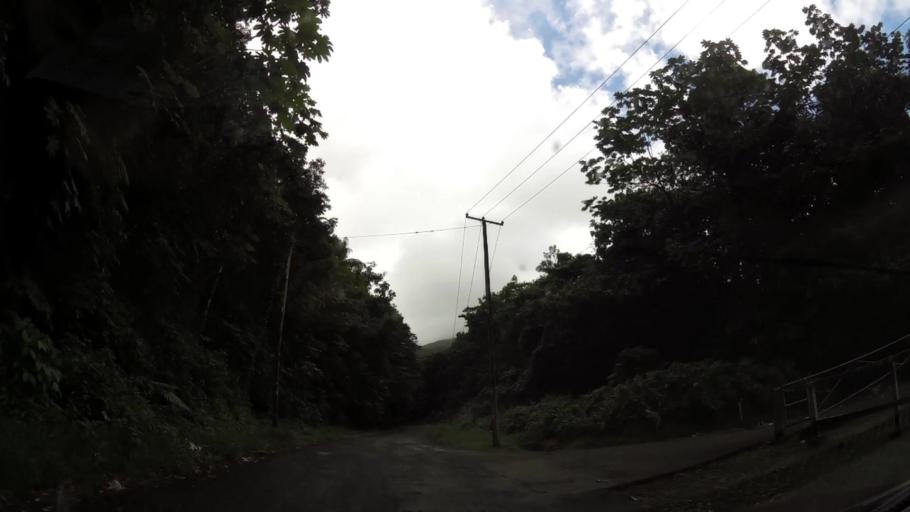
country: DM
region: Saint Paul
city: Pont Casse
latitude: 15.3944
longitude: -61.3105
